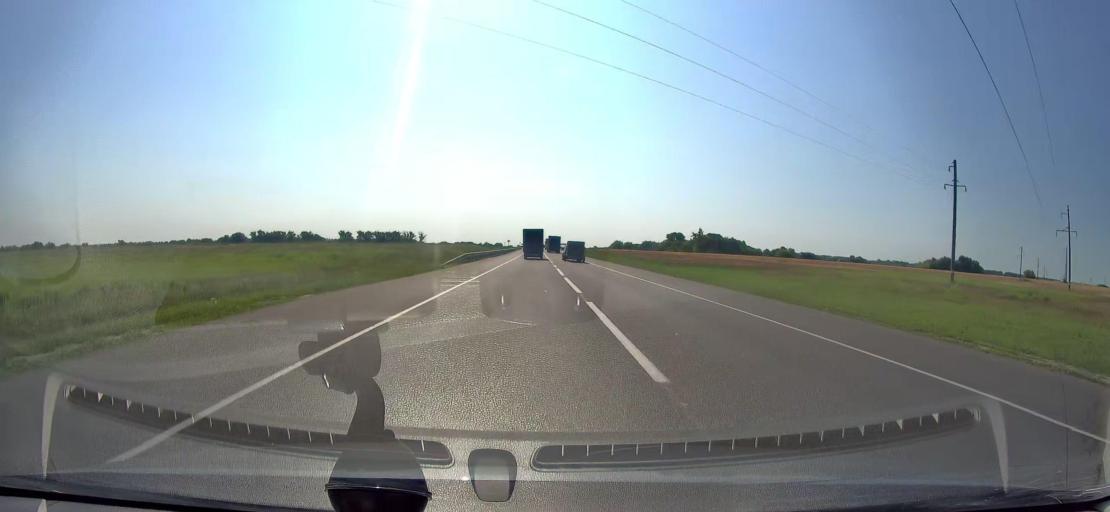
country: RU
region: Orjol
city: Kromy
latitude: 52.6521
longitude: 35.7306
